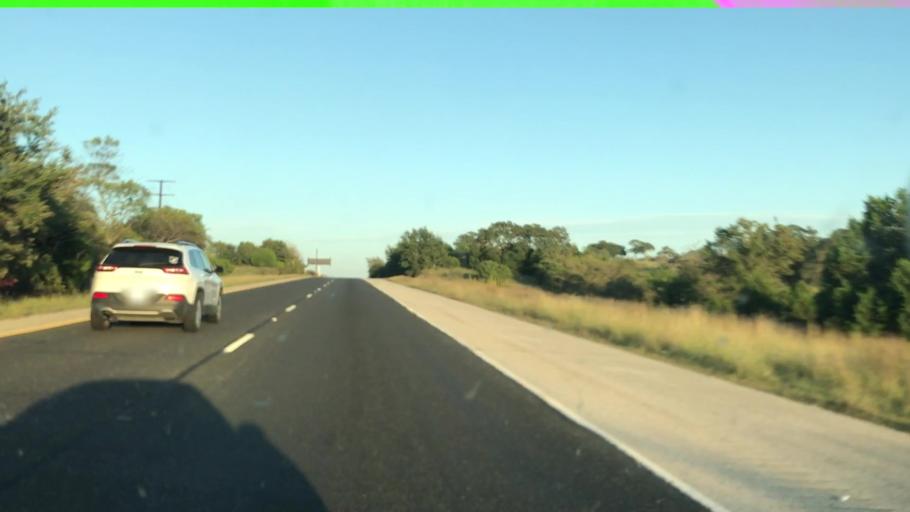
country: US
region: Texas
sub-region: Kerr County
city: Kerrville
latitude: 30.0677
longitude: -99.0635
